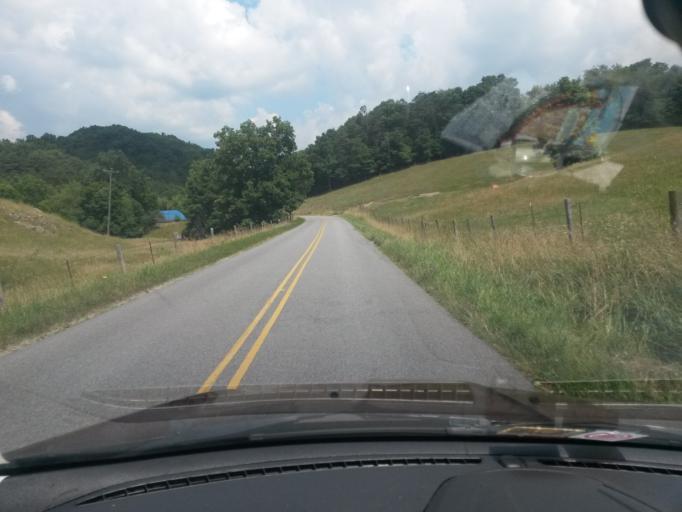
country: US
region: Virginia
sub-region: Giles County
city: Narrows
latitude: 37.3892
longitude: -80.7913
